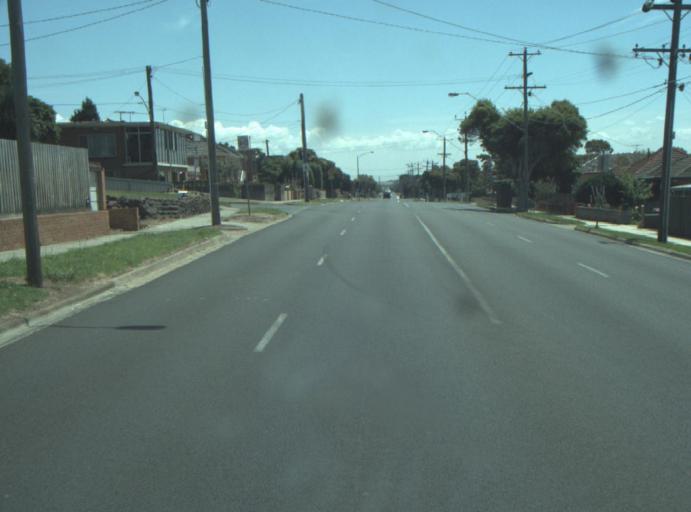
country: AU
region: Victoria
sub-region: Greater Geelong
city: Bell Park
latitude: -38.1077
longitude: 144.3321
